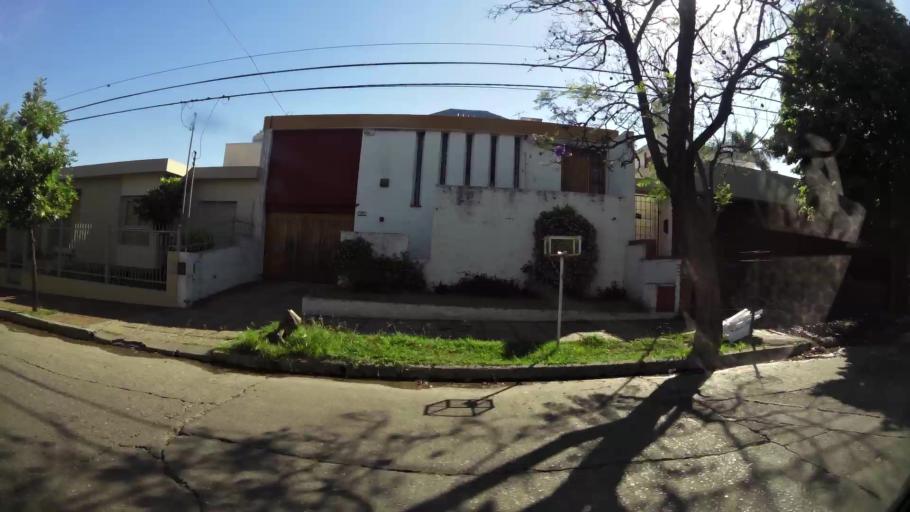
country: AR
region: Cordoba
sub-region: Departamento de Capital
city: Cordoba
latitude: -31.4274
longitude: -64.1619
